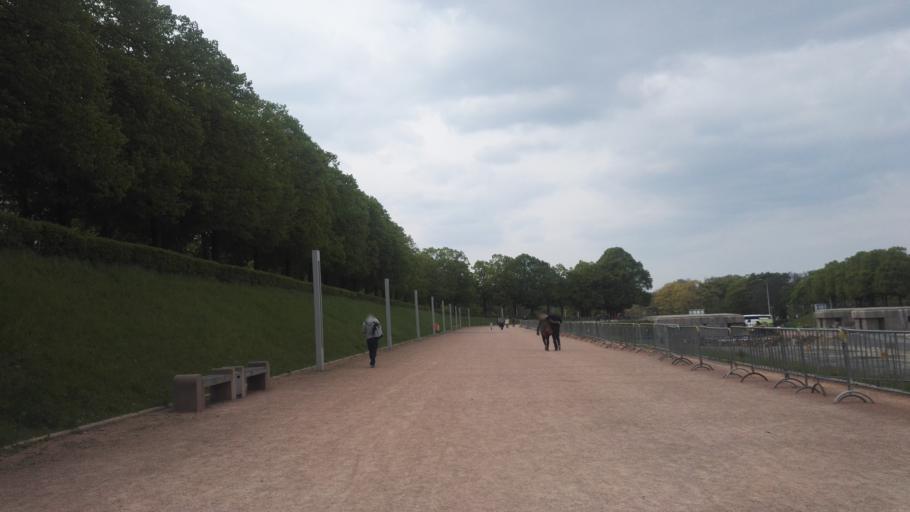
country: DE
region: Saxony
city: Leipzig
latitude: 51.3125
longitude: 12.4118
